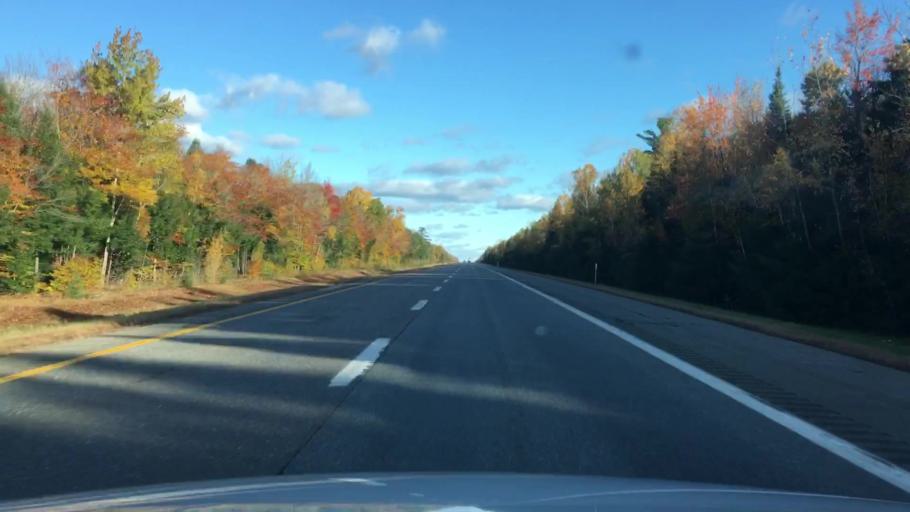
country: US
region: Maine
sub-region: Penobscot County
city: Greenbush
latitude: 45.0686
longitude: -68.6899
